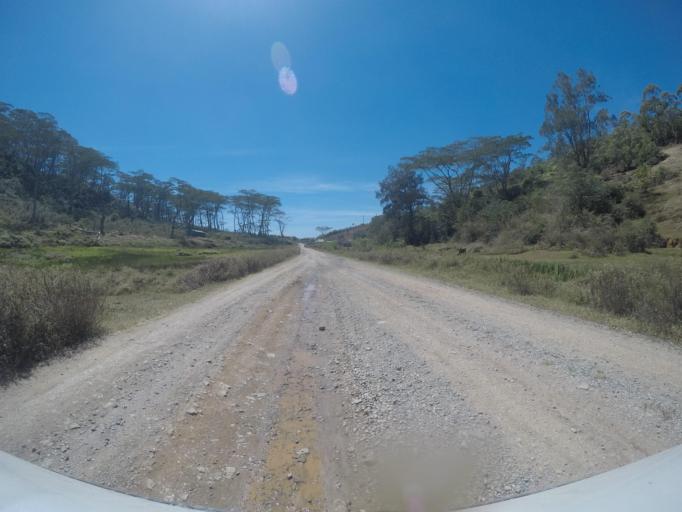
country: TL
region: Ermera
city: Gleno
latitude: -8.7744
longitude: 125.3941
